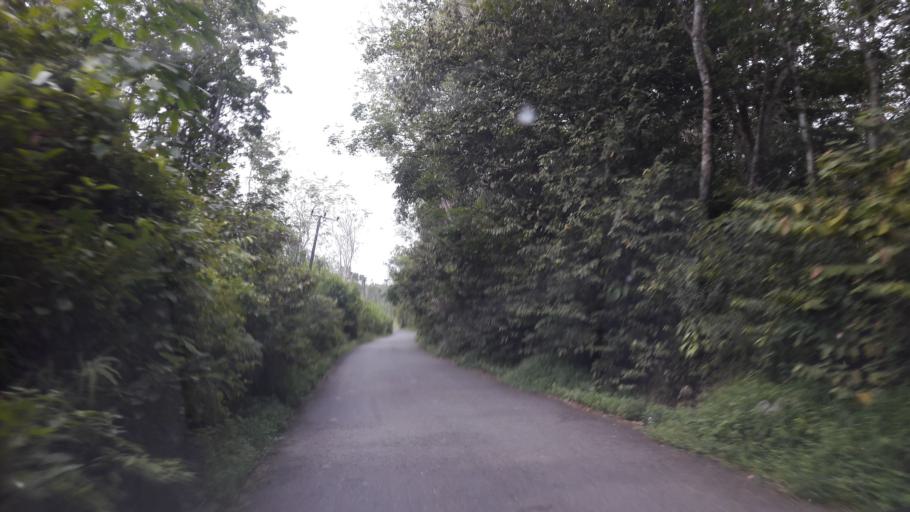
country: ID
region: South Sumatra
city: Gunungmenang
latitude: -3.1256
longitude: 104.1127
